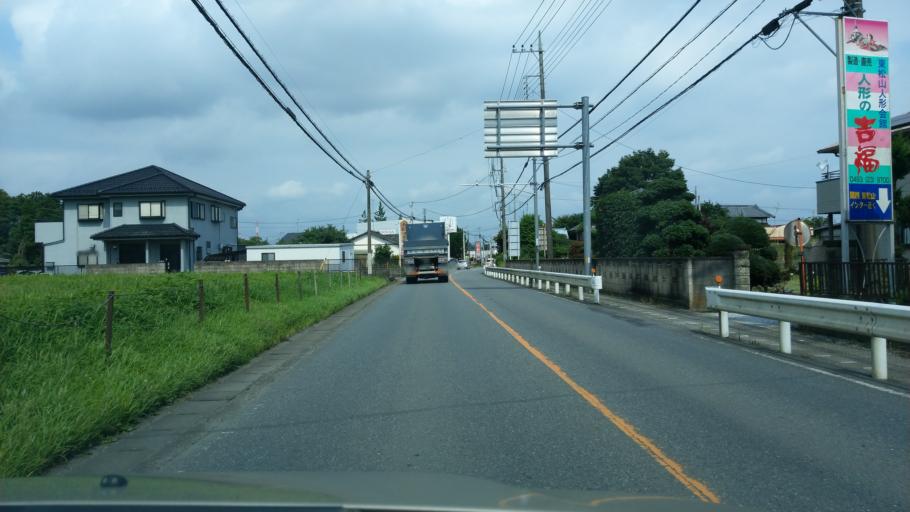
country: JP
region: Saitama
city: Ogawa
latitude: 36.0330
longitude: 139.3470
